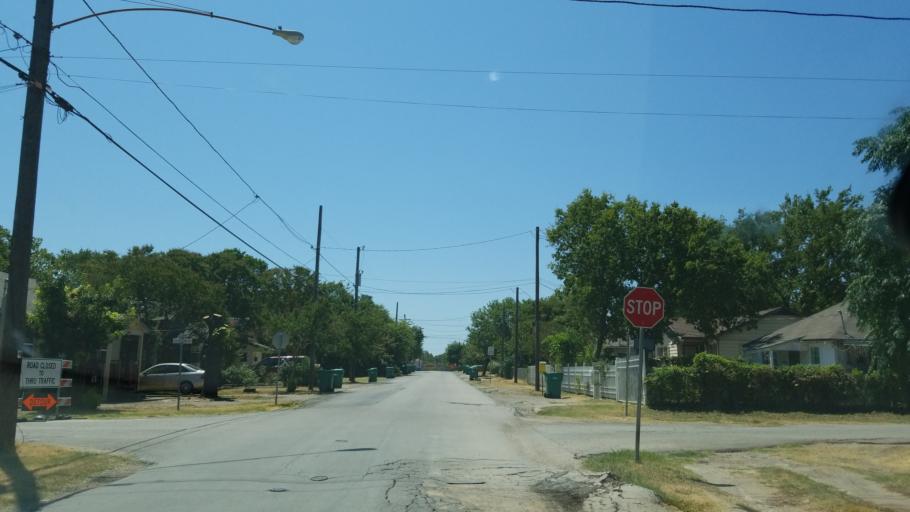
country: US
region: Texas
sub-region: Dallas County
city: Cockrell Hill
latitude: 32.7400
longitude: -96.8927
